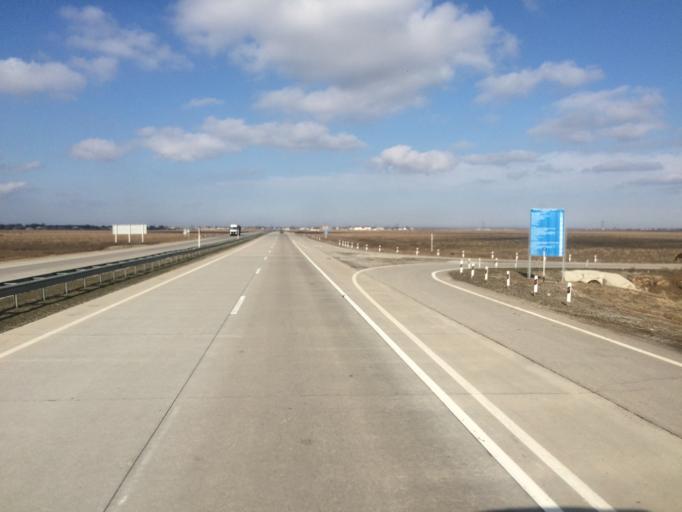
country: KZ
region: Ongtustik Qazaqstan
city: Temirlanovka
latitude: 42.7753
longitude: 69.2064
